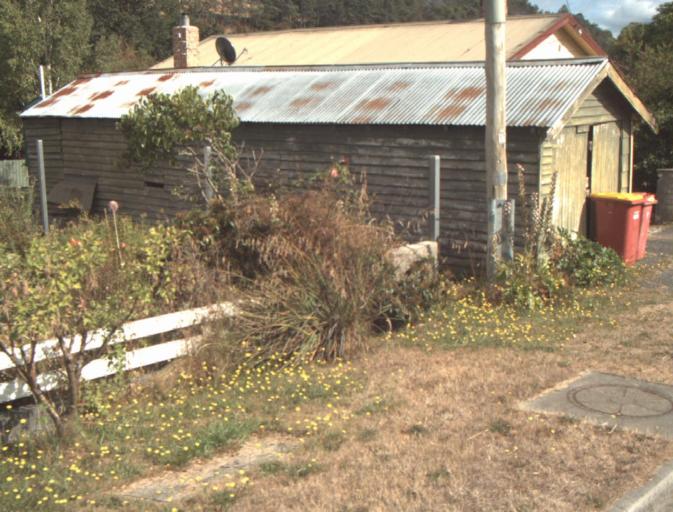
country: AU
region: Tasmania
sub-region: Launceston
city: Mayfield
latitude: -41.2618
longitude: 147.2178
